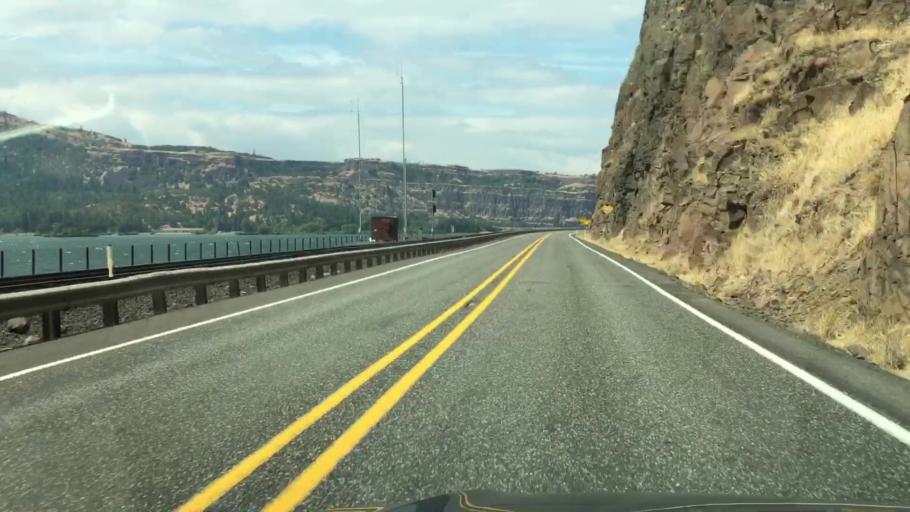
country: US
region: Oregon
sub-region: Wasco County
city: Chenoweth
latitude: 45.6864
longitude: -121.2678
